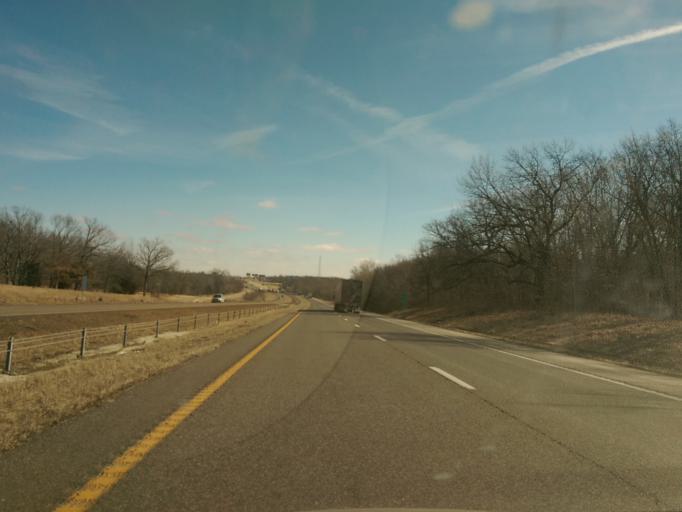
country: US
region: Missouri
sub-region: Boone County
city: Hallsville
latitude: 38.9557
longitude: -92.1598
